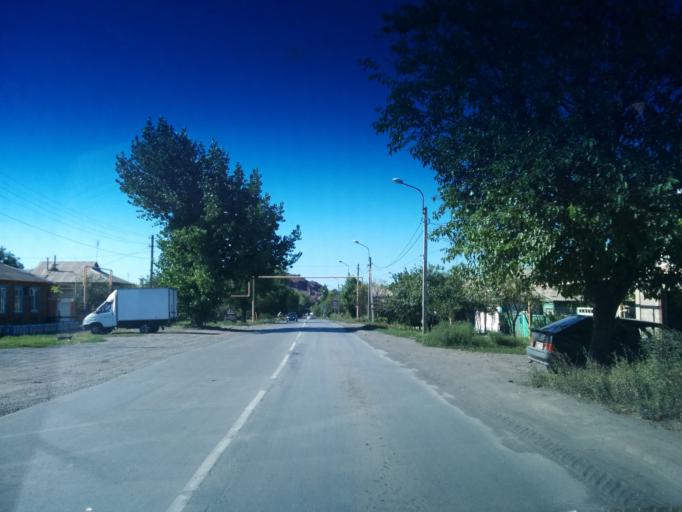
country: RU
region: Rostov
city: Shakhty
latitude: 47.6887
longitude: 40.2637
